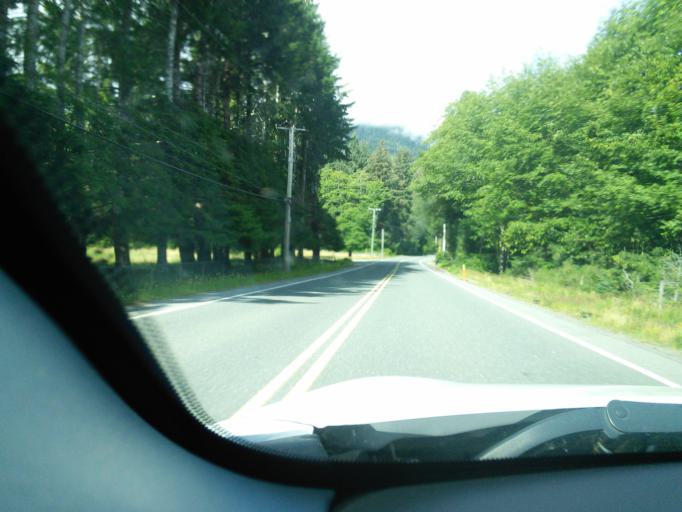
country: CA
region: British Columbia
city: Campbell River
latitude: 50.3615
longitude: -125.9226
